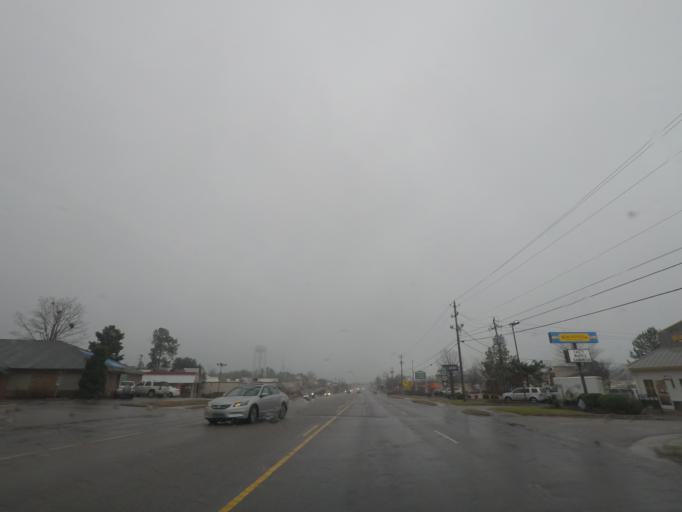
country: US
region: North Carolina
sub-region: Moore County
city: Southern Pines
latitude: 35.1569
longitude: -79.4138
